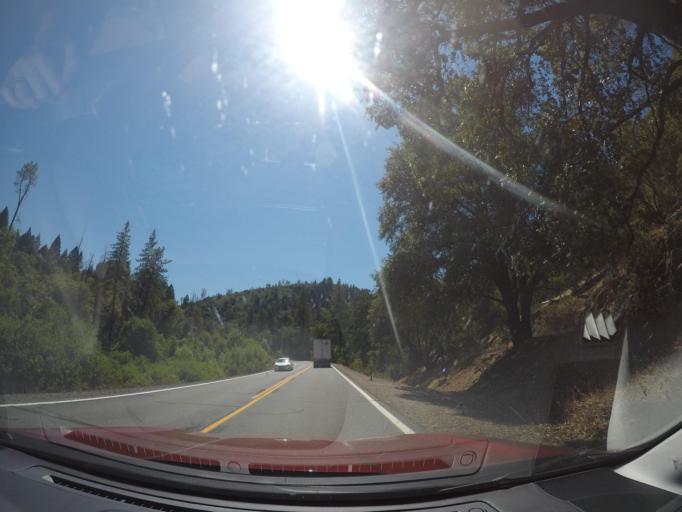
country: US
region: California
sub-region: Shasta County
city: Bella Vista
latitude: 40.7423
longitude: -122.0691
